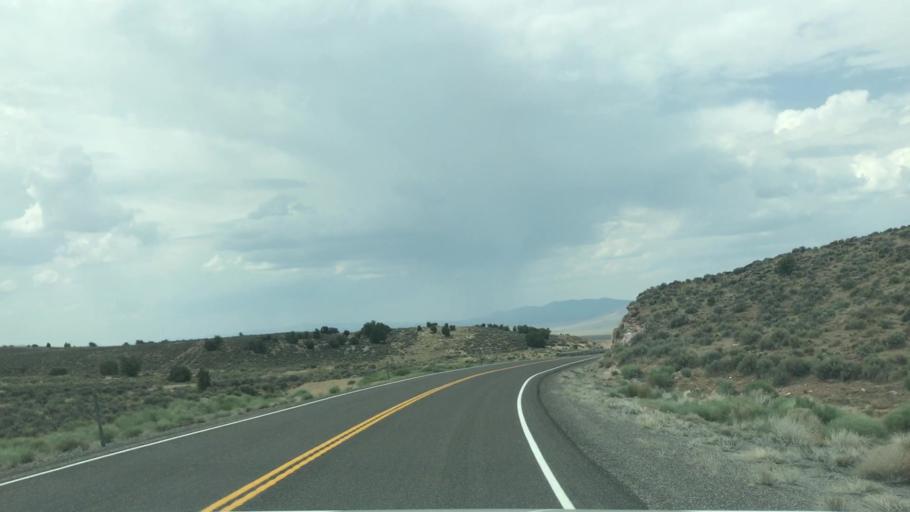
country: US
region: Nevada
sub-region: Eureka County
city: Eureka
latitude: 39.4001
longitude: -115.7060
